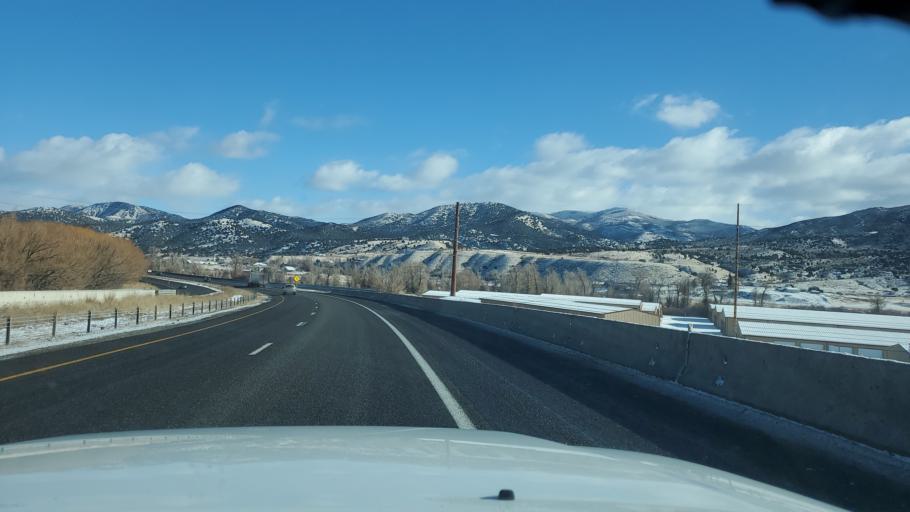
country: US
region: Utah
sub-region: Summit County
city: Coalville
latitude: 40.8091
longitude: -111.4042
